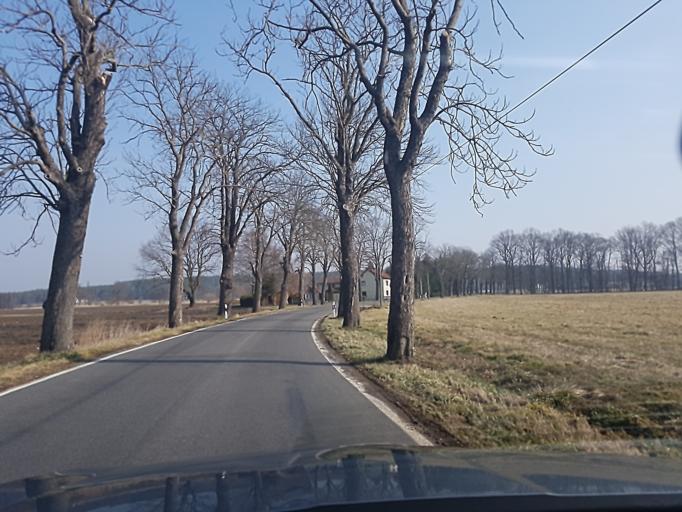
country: DE
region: Brandenburg
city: Falkenberg
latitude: 51.6382
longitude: 13.2882
